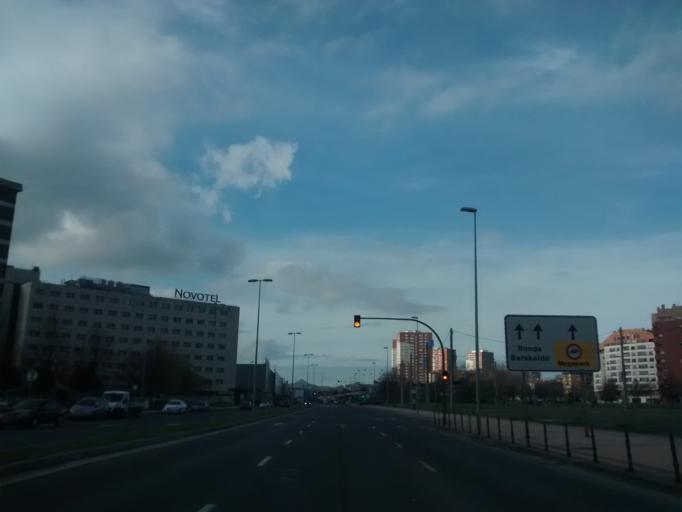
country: ES
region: Basque Country
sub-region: Bizkaia
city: Barakaldo
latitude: 43.2865
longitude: -2.9963
